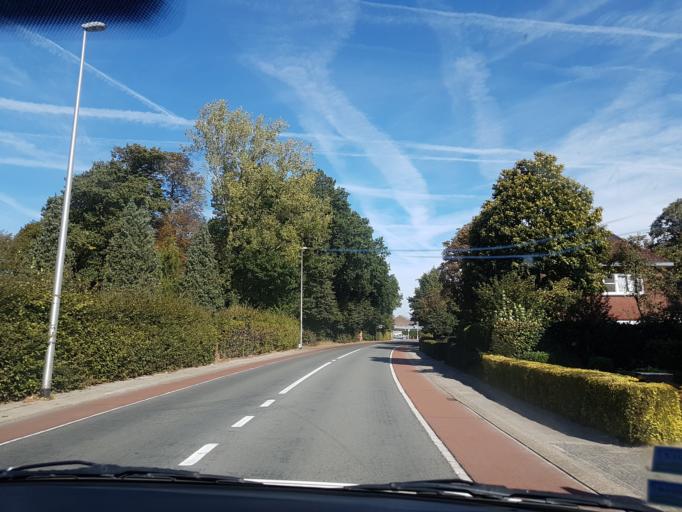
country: BE
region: Flanders
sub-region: Provincie Limburg
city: Overpelt
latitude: 51.2030
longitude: 5.4048
